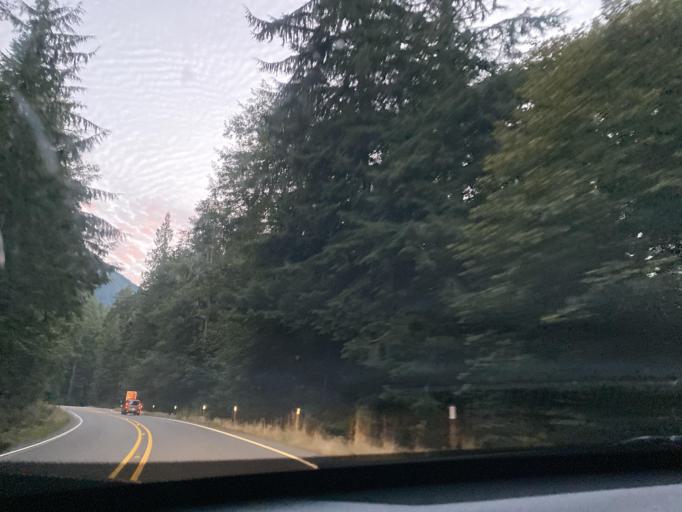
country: CA
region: British Columbia
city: Sooke
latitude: 48.0576
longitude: -123.7878
